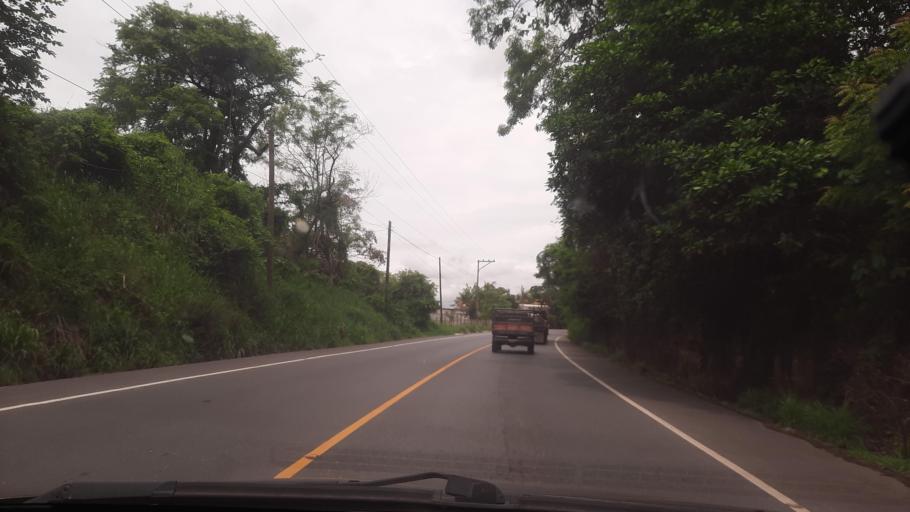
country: GT
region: Zacapa
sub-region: Municipio de Zacapa
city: Gualan
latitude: 15.1458
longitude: -89.3274
